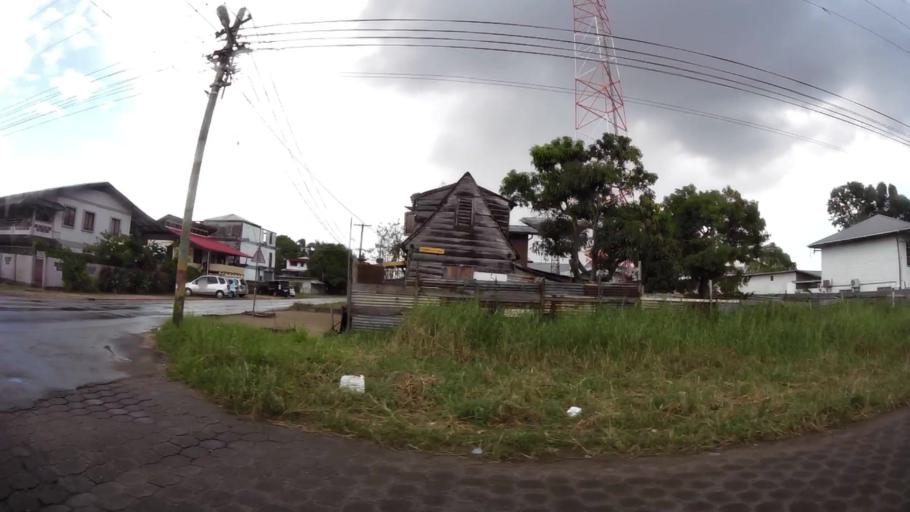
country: SR
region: Paramaribo
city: Paramaribo
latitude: 5.8319
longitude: -55.1463
